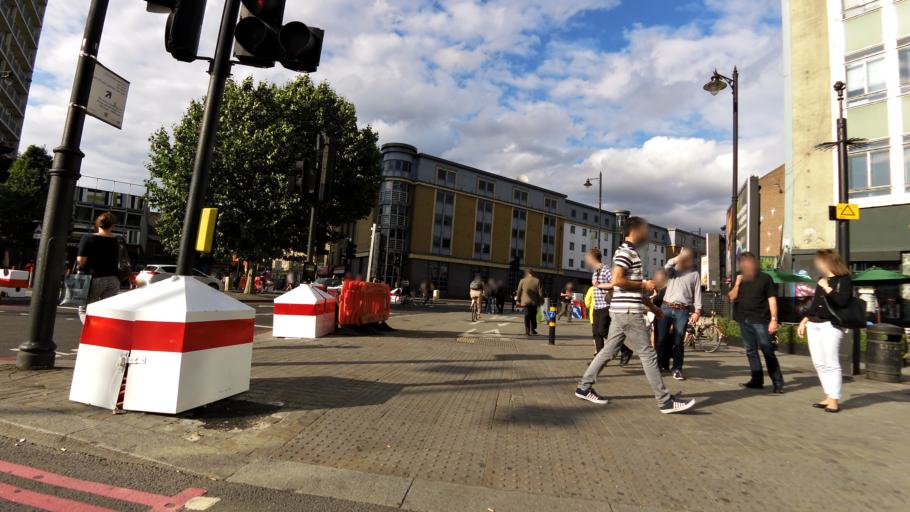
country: GB
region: England
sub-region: Greater London
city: Barbican
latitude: 51.5262
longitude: -0.0838
